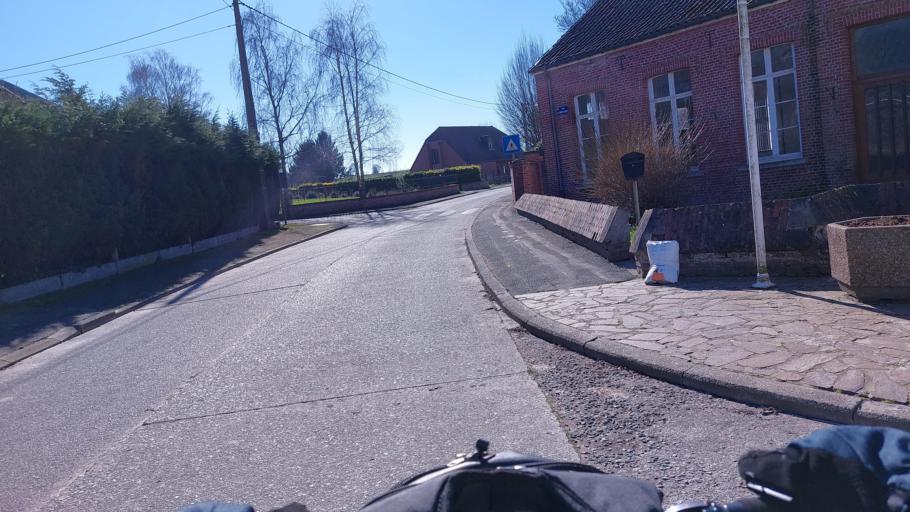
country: BE
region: Wallonia
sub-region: Province du Hainaut
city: Brugelette
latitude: 50.6066
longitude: 3.8906
